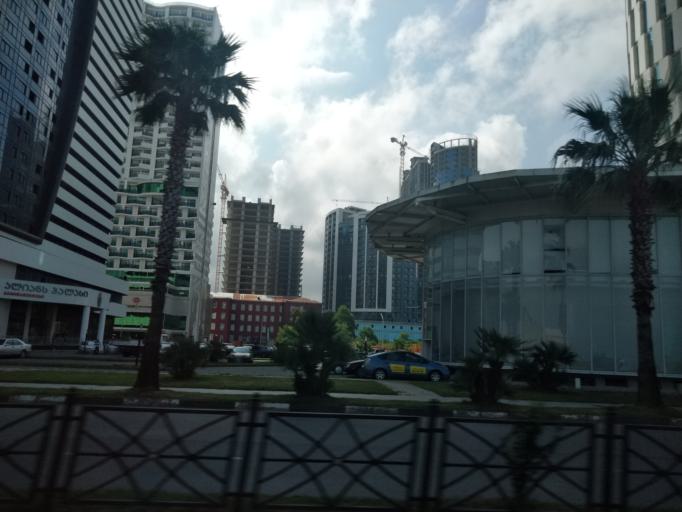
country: GE
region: Ajaria
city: Batumi
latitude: 41.6417
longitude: 41.6151
